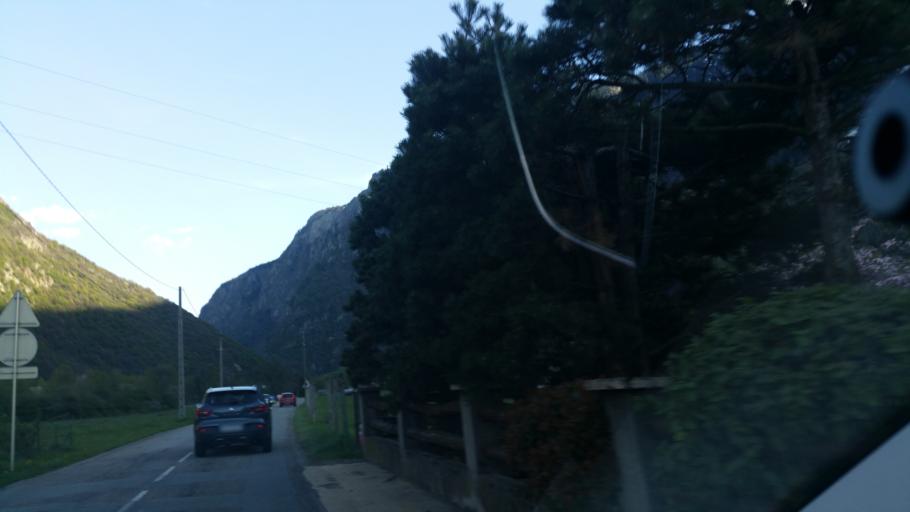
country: FR
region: Rhone-Alpes
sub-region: Departement de la Savoie
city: La Chambre
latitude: 45.3293
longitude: 6.3139
